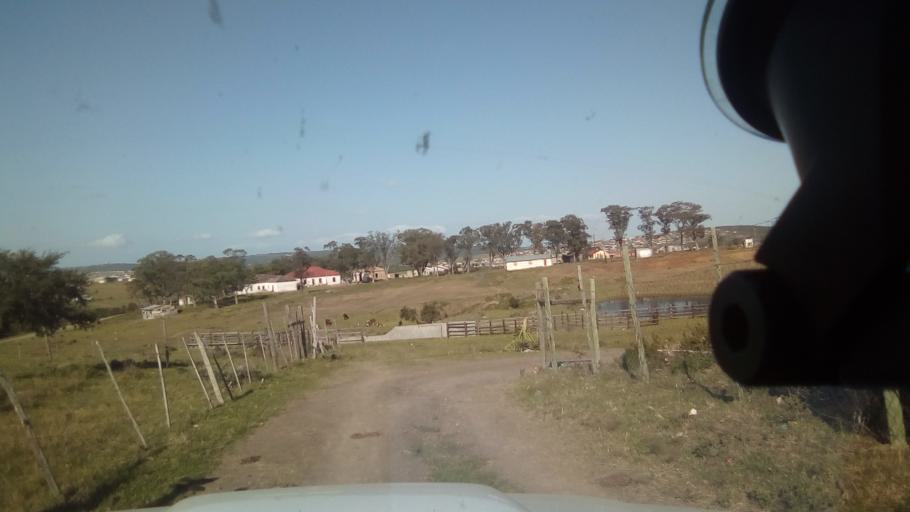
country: ZA
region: Eastern Cape
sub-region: Buffalo City Metropolitan Municipality
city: Bhisho
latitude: -32.8137
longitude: 27.3578
